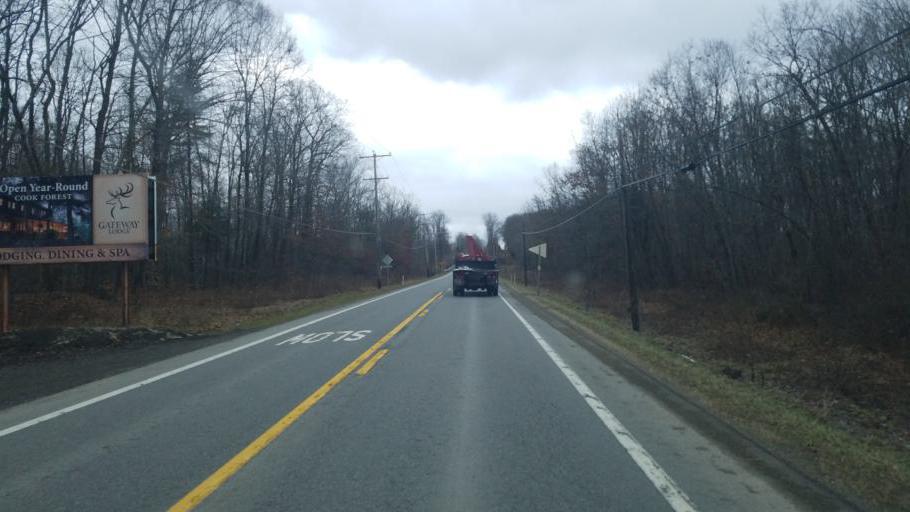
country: US
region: Pennsylvania
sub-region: Clarion County
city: Marianne
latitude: 41.3609
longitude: -79.3204
